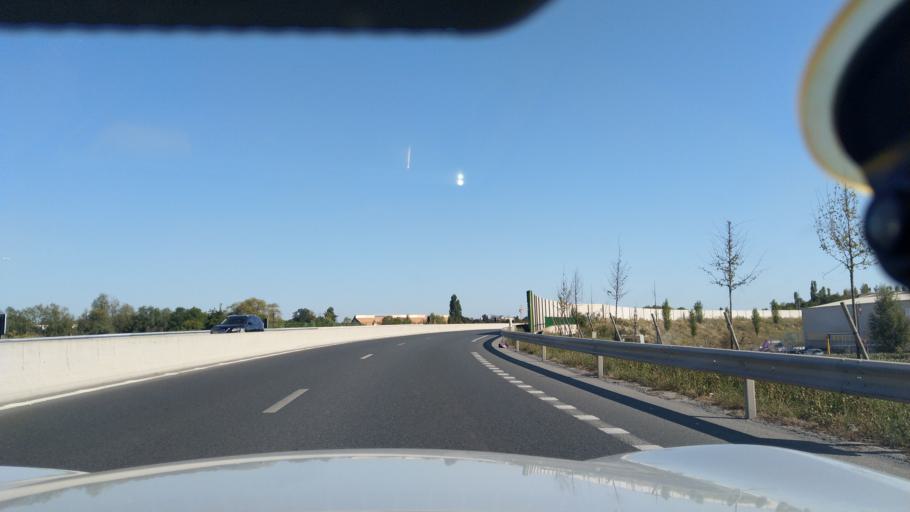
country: FR
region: Ile-de-France
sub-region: Departement du Val-d'Oise
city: Arnouville
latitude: 48.9748
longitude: 2.4265
